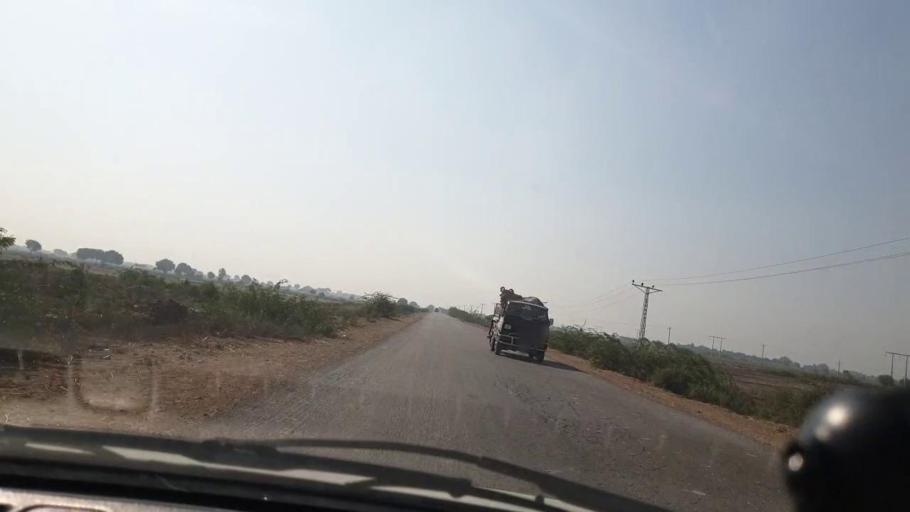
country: PK
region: Sindh
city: Bulri
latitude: 24.9165
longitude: 68.3494
